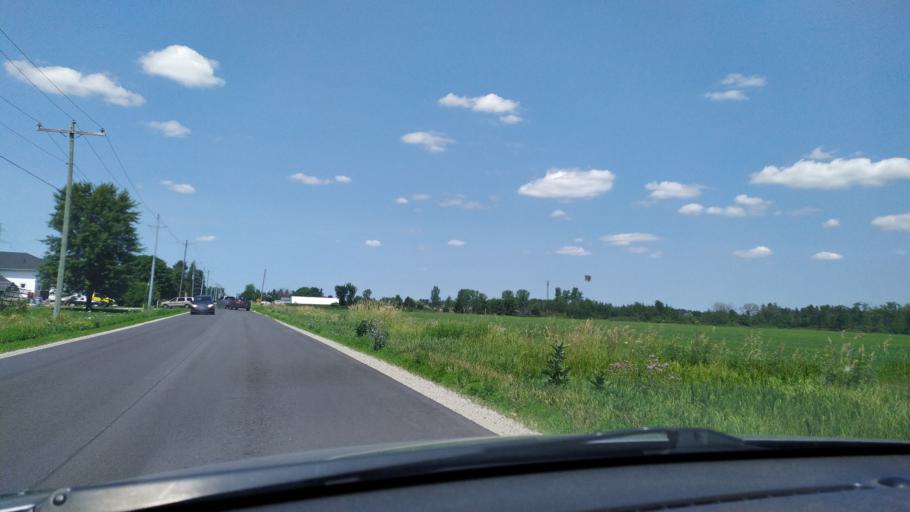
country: CA
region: Ontario
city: Stratford
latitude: 43.3627
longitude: -80.9377
